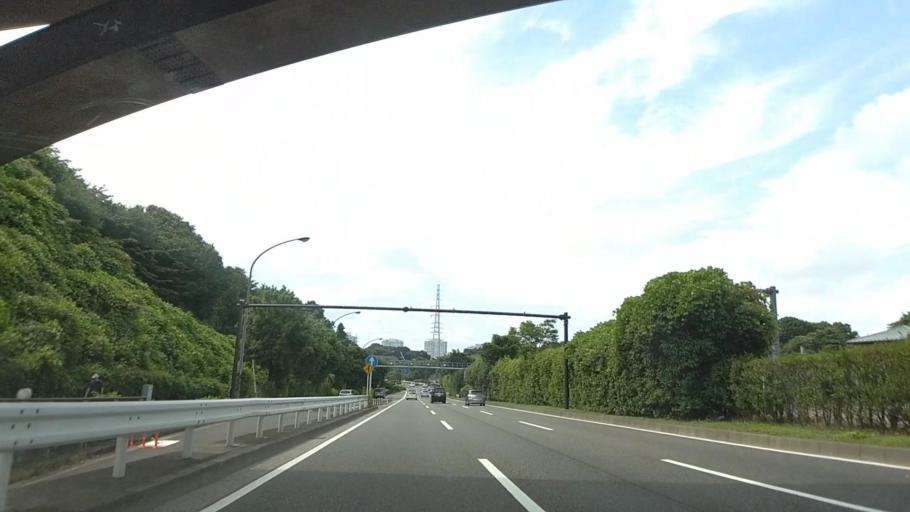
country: JP
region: Kanagawa
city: Yokohama
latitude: 35.4411
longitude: 139.5604
